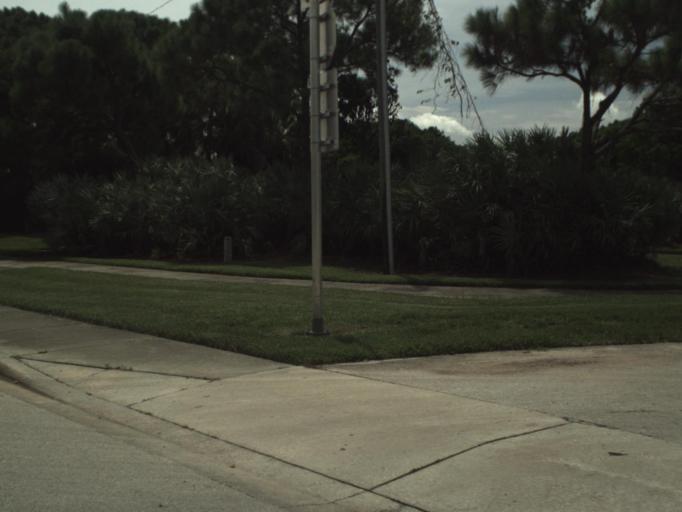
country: US
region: Florida
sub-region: Palm Beach County
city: Palm Beach Gardens
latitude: 26.8389
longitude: -80.1276
